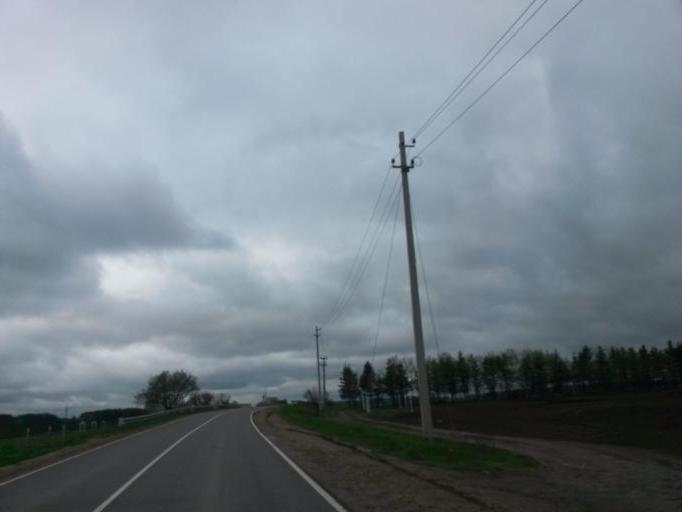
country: RU
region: Moskovskaya
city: Klimovsk
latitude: 55.3430
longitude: 37.5889
